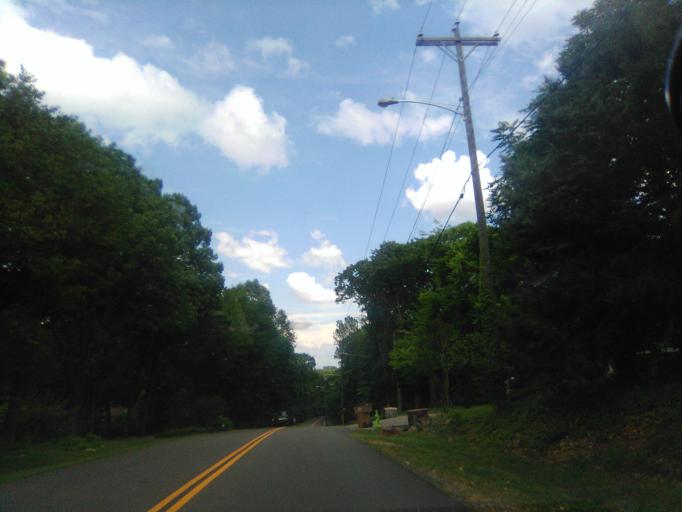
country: US
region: Tennessee
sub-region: Davidson County
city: Belle Meade
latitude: 36.1289
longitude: -86.8755
